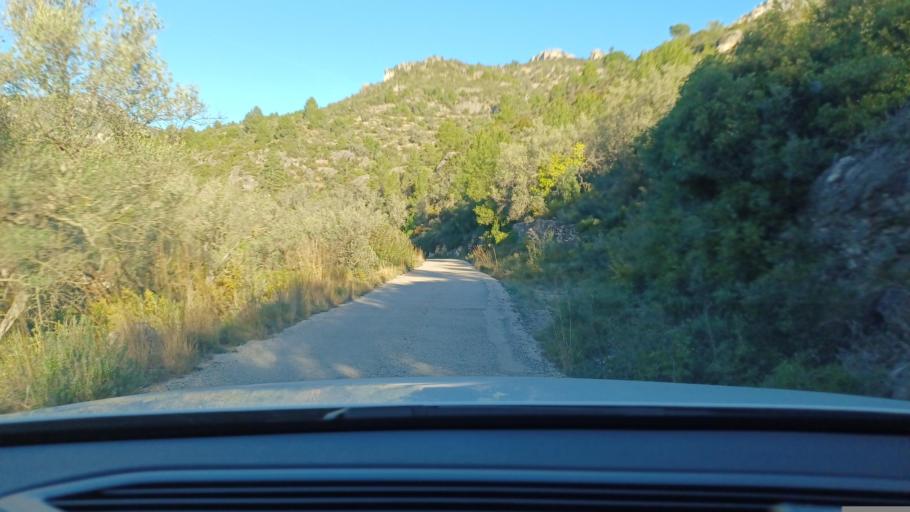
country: ES
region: Catalonia
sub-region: Provincia de Tarragona
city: Mas de Barberans
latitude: 40.7201
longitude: 0.3473
